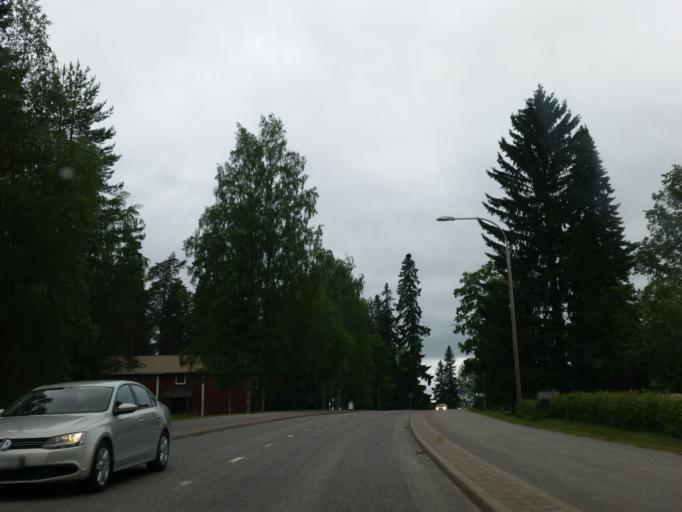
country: FI
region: Northern Savo
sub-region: Koillis-Savo
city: Kaavi
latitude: 62.9743
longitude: 28.4877
